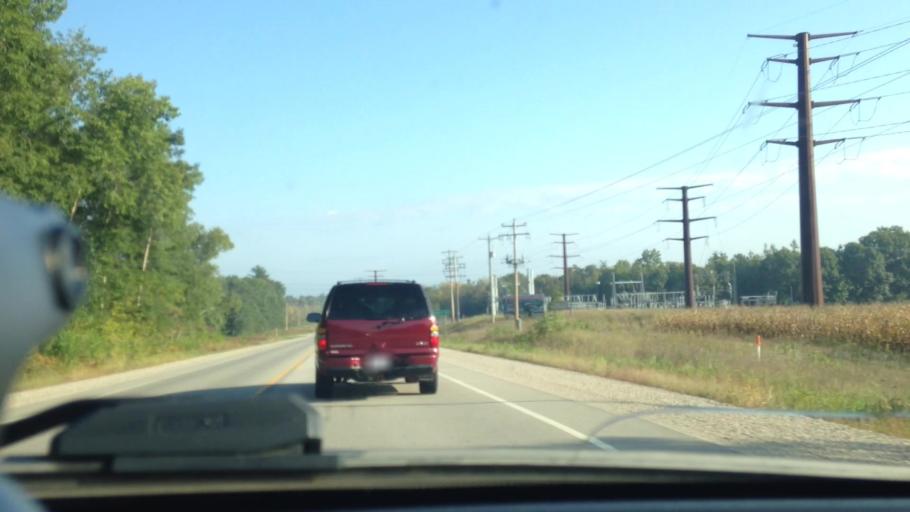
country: US
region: Wisconsin
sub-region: Marinette County
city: Peshtigo
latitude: 45.1746
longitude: -87.9960
